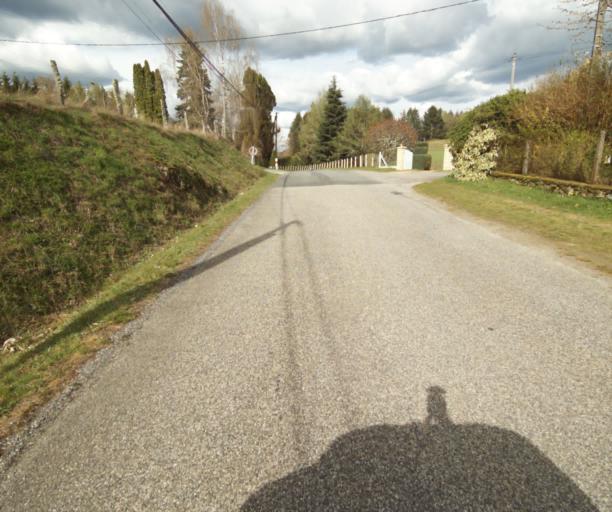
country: FR
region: Limousin
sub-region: Departement de la Correze
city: Argentat
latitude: 45.2116
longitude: 1.9671
